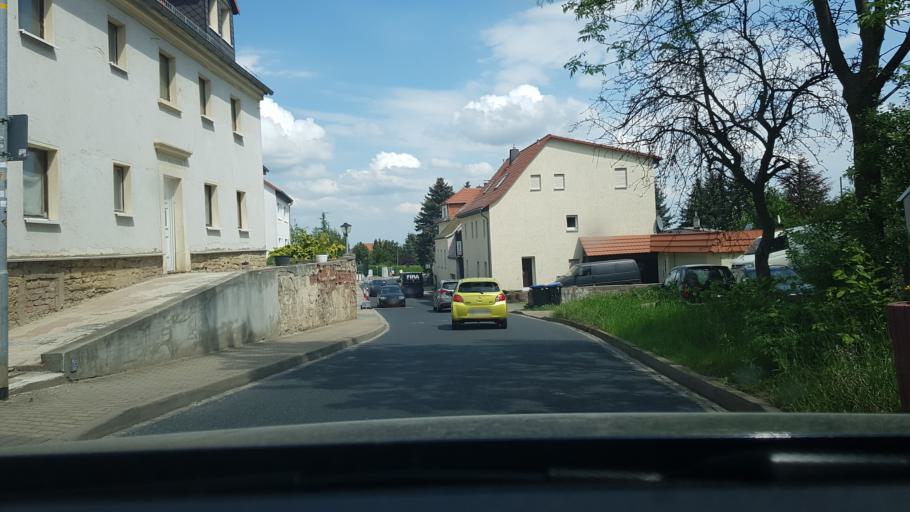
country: DE
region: Saxony
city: Freital
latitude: 51.0298
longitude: 13.6611
